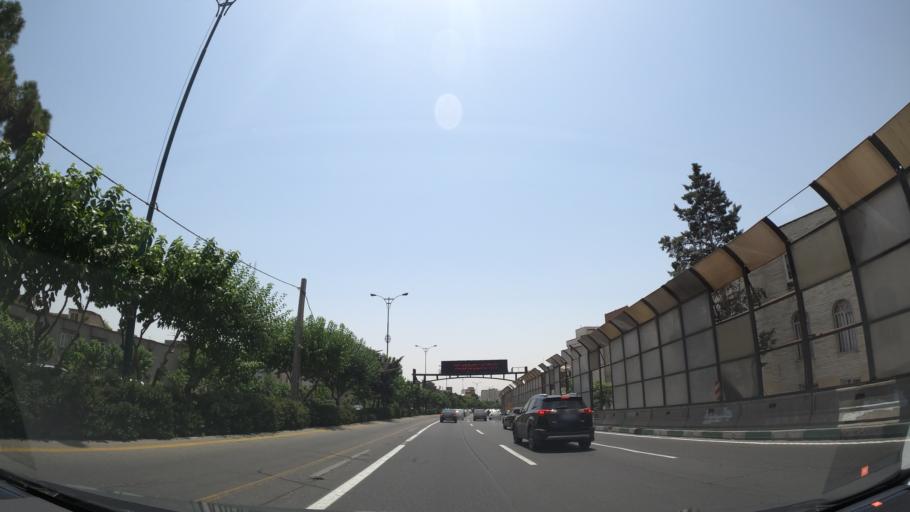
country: IR
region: Tehran
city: Tehran
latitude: 35.7291
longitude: 51.3832
